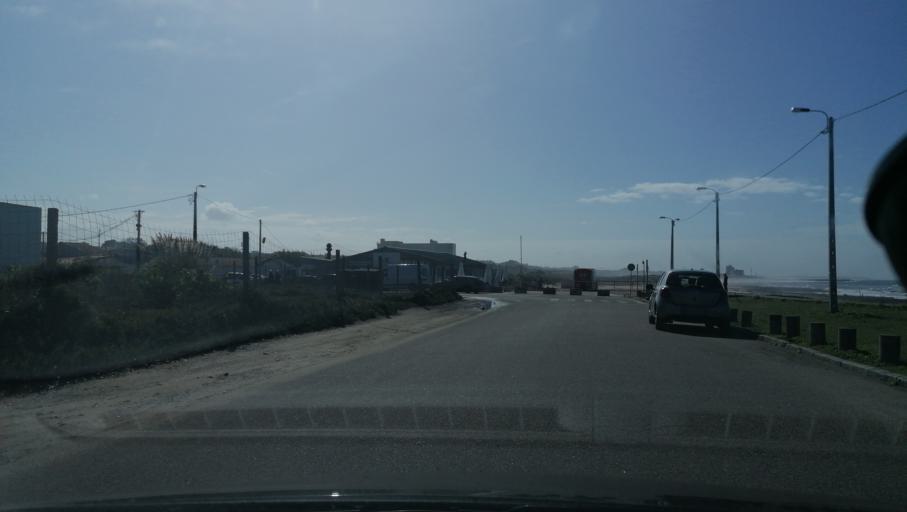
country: PT
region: Porto
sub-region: Vila Nova de Gaia
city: Arcozelo
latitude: 41.0345
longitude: -8.6469
